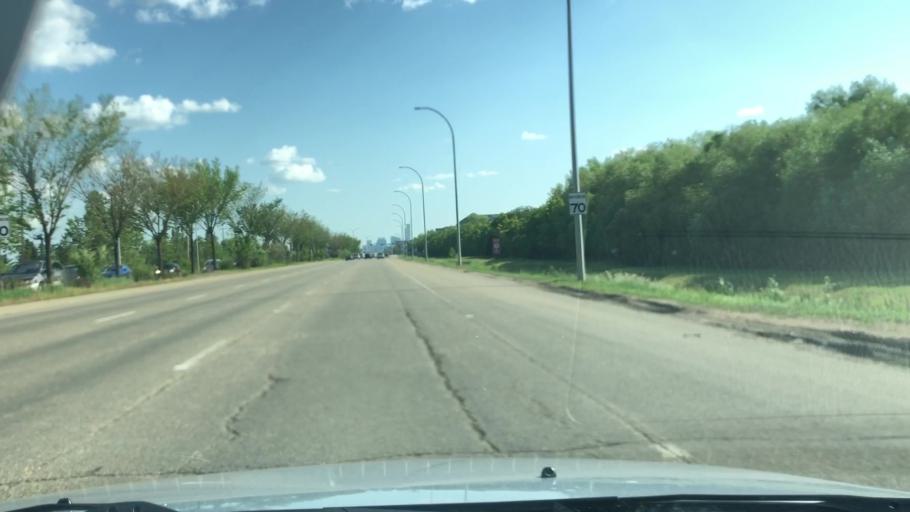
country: CA
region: Alberta
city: Edmonton
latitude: 53.6062
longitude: -113.4920
